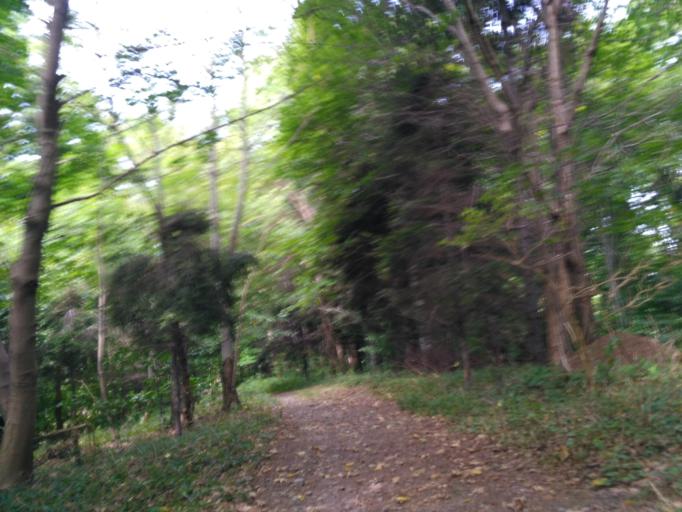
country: PL
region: Subcarpathian Voivodeship
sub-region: Powiat strzyzowski
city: Frysztak
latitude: 49.8907
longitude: 21.5549
